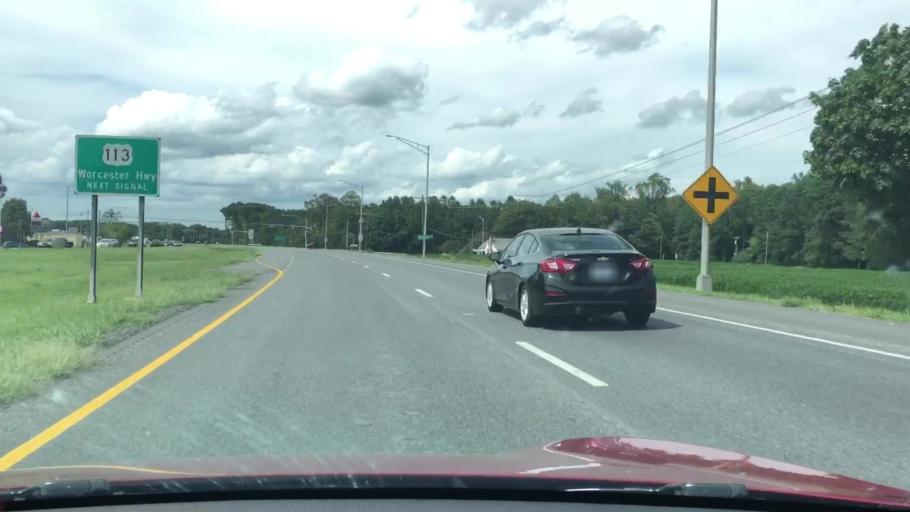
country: US
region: Maryland
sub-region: Worcester County
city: Pocomoke City
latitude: 38.0595
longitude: -75.5439
